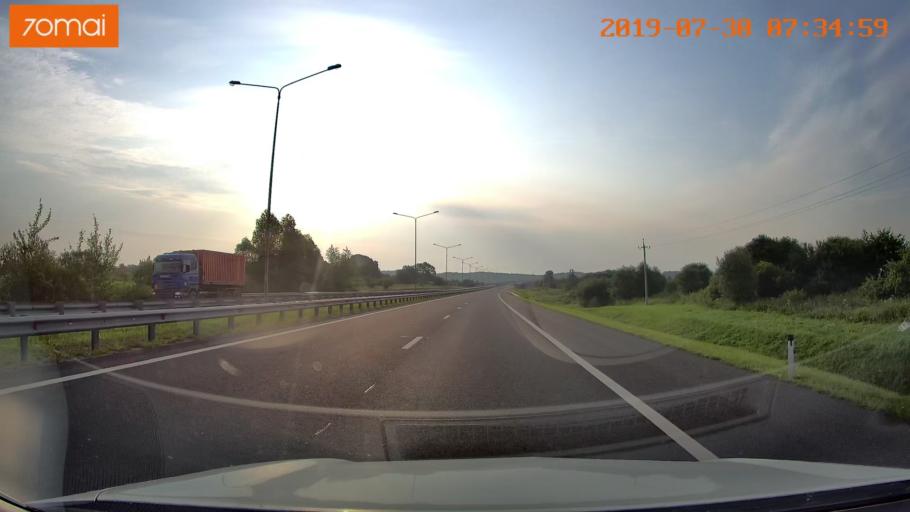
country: RU
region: Kaliningrad
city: Gvardeysk
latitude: 54.6726
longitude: 21.0869
